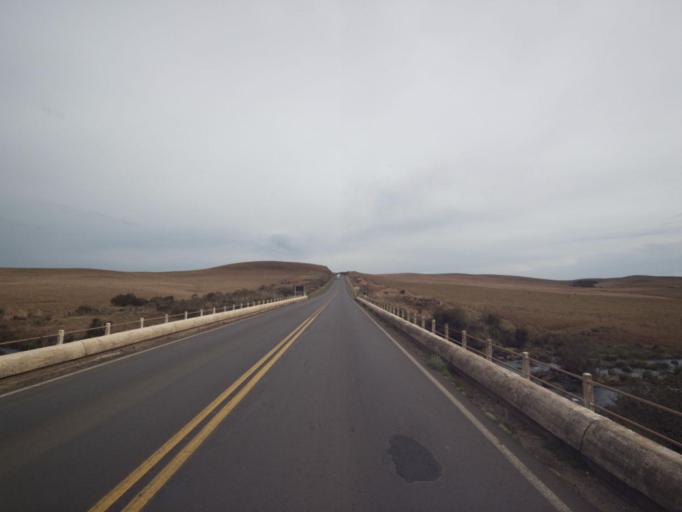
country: BR
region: Parana
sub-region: Palmas
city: Palmas
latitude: -26.7103
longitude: -51.6070
